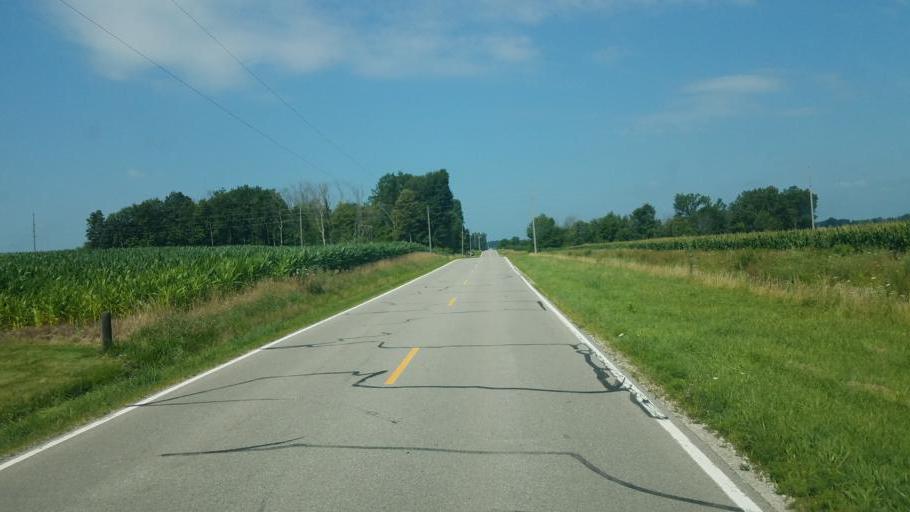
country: US
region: Ohio
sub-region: Crawford County
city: Galion
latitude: 40.7561
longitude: -82.8273
